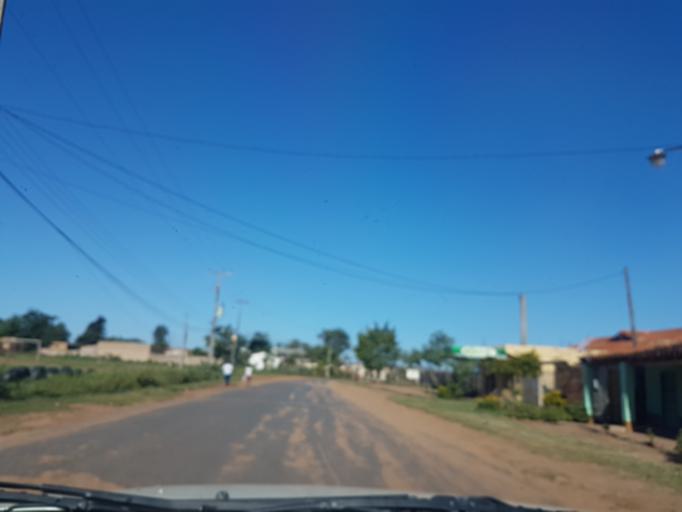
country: PY
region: Cordillera
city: Tobati
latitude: -25.2640
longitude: -57.0952
